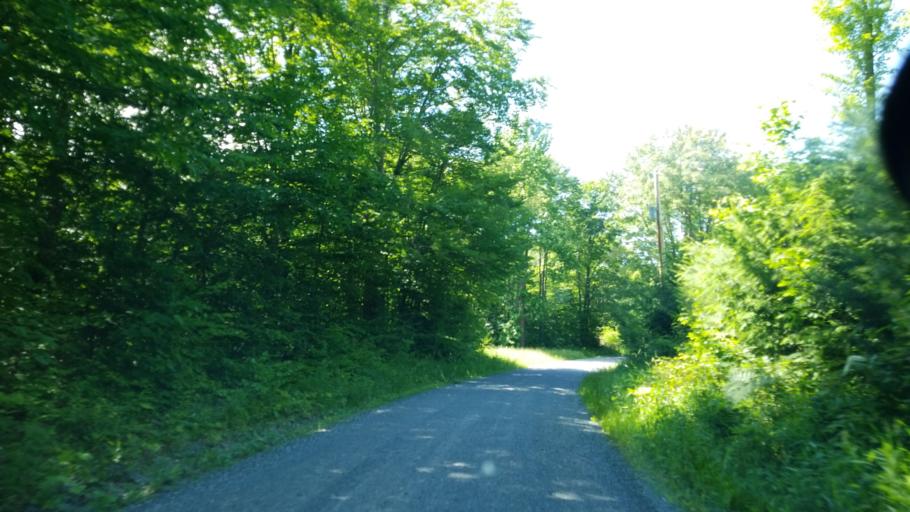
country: US
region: Pennsylvania
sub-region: Clearfield County
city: Clearfield
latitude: 41.1924
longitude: -78.4811
